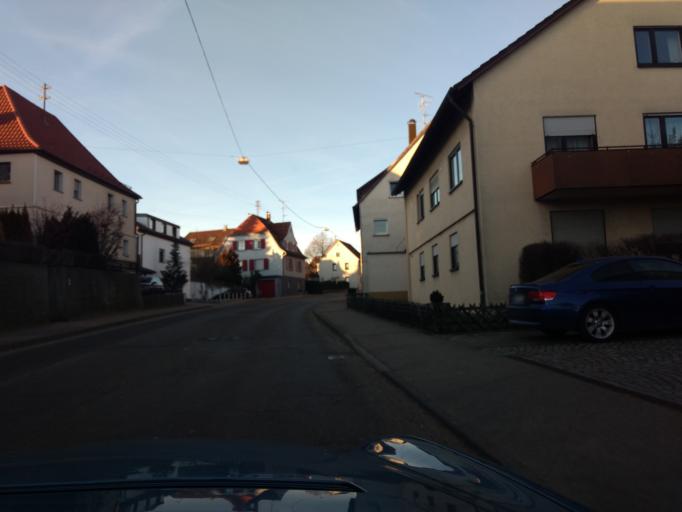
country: DE
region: Baden-Wuerttemberg
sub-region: Regierungsbezirk Stuttgart
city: Schwabisch Gmund
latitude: 48.7808
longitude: 9.7962
